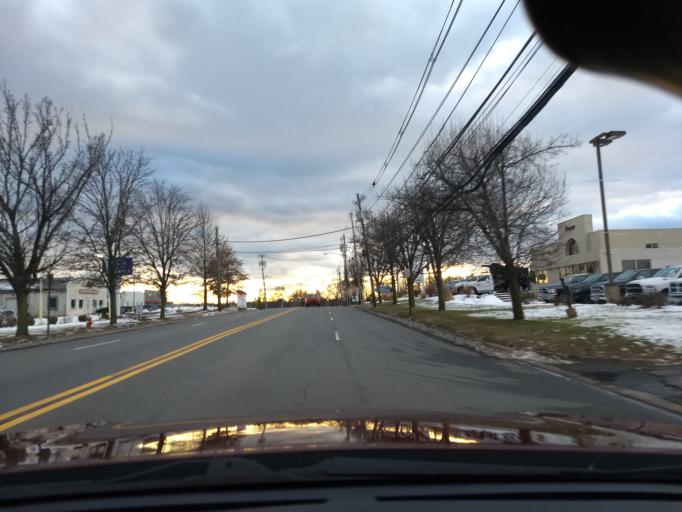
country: US
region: New Jersey
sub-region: Morris County
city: Morristown
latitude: 40.8066
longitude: -74.4630
